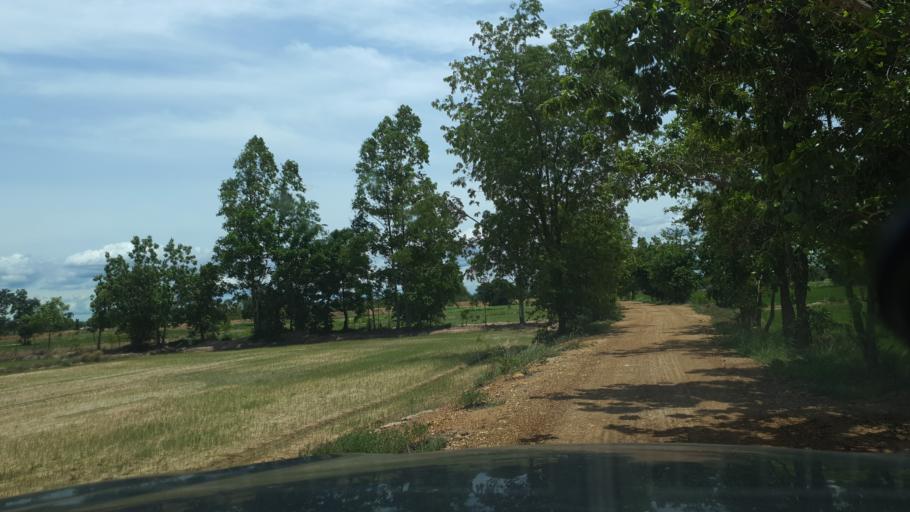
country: TH
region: Sukhothai
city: Ban Na
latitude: 17.1336
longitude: 99.6700
